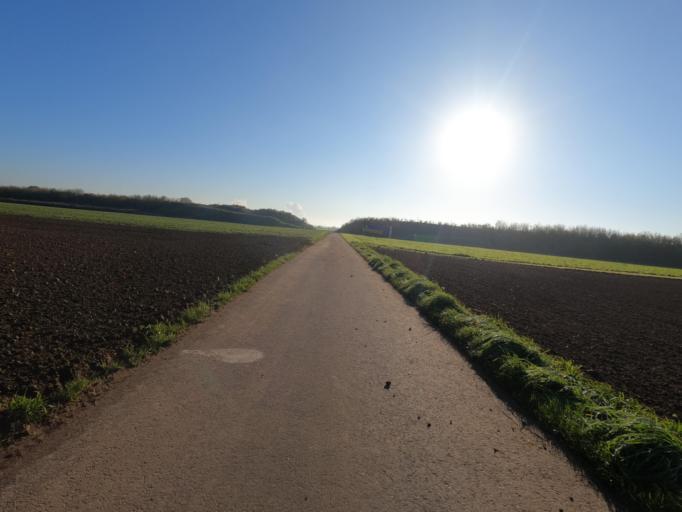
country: DE
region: North Rhine-Westphalia
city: Erkelenz
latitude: 51.0840
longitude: 6.3737
